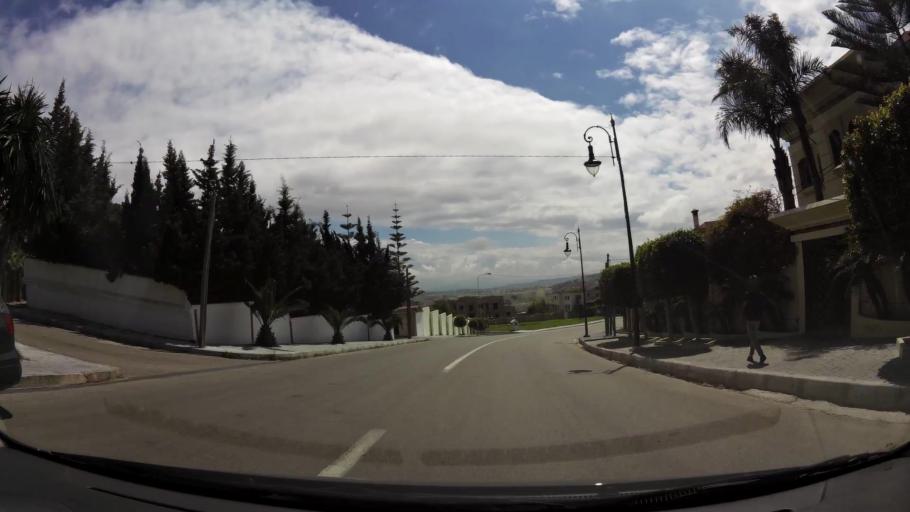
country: MA
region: Tanger-Tetouan
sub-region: Tanger-Assilah
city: Boukhalef
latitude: 35.7814
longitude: -5.8605
